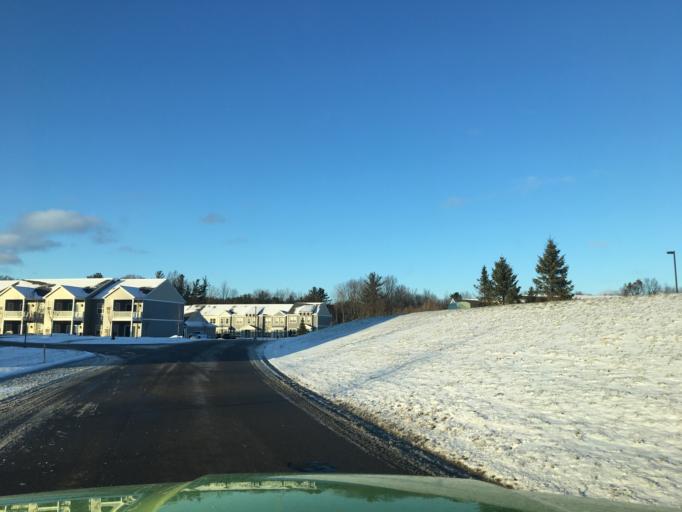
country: US
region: Michigan
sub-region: Kent County
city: Rockford
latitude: 43.1219
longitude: -85.5990
